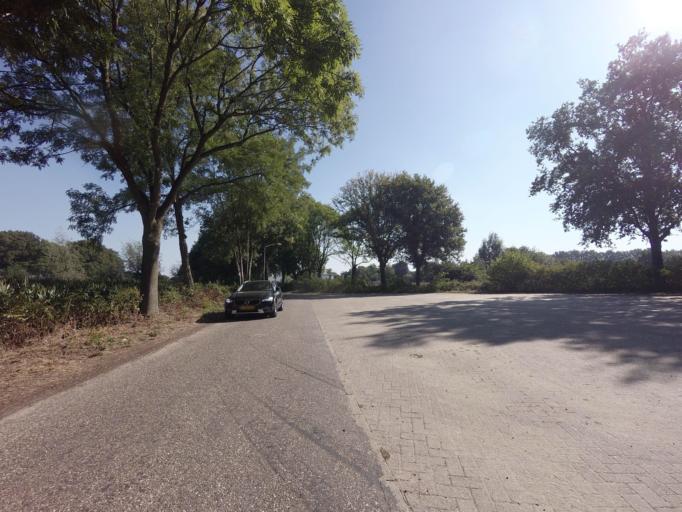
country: NL
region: North Brabant
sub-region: Gemeente Someren
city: Someren
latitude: 51.3911
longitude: 5.6933
